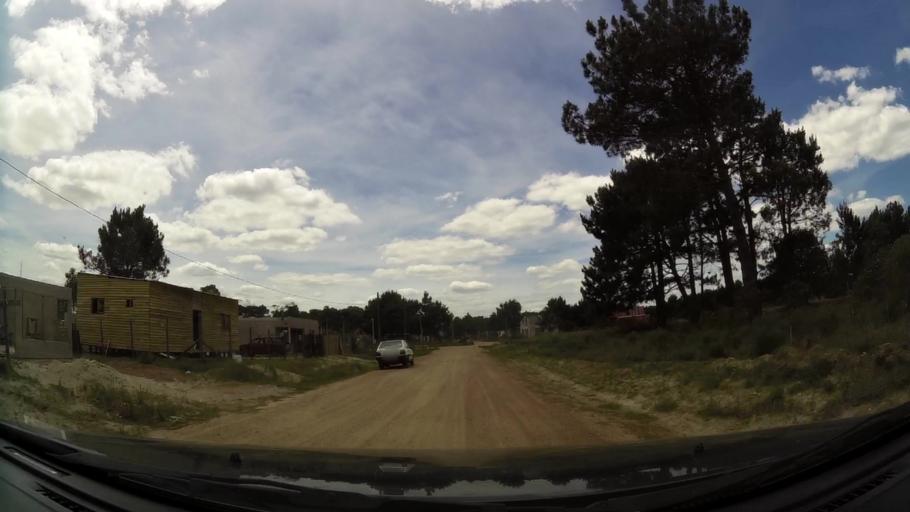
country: UY
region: Canelones
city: Pando
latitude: -34.8066
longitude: -55.9430
